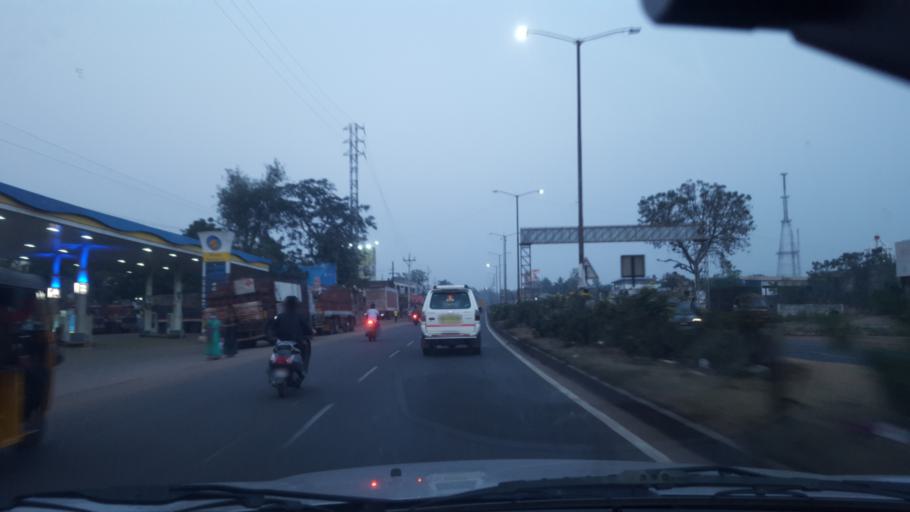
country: IN
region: Andhra Pradesh
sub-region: East Godavari
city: Rajahmundry
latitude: 17.0265
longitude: 81.8074
